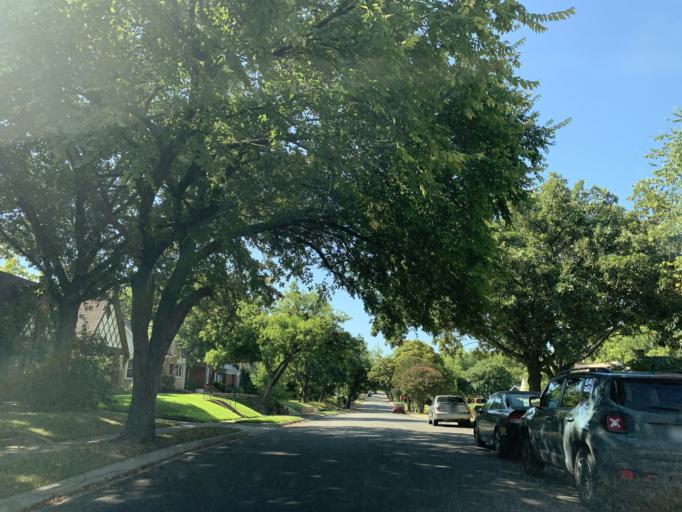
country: US
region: Texas
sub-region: Dallas County
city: Cockrell Hill
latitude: 32.7443
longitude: -96.8655
